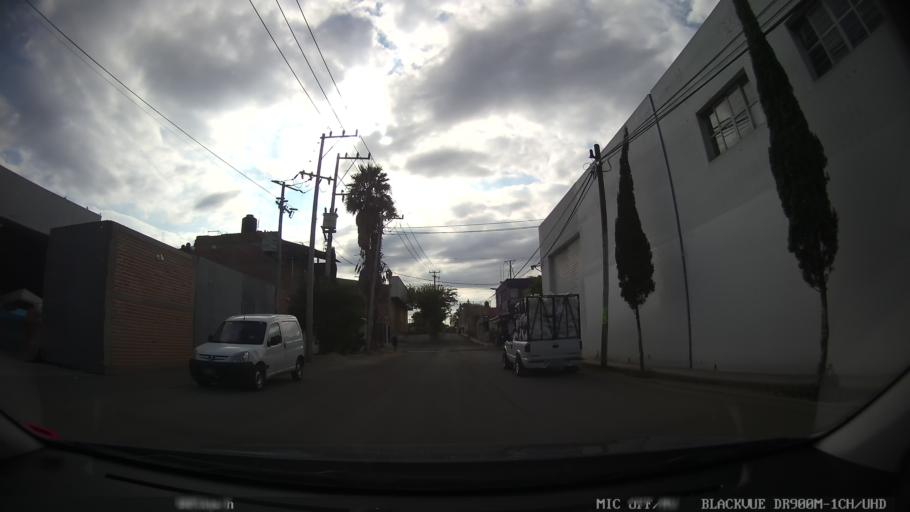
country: MX
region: Jalisco
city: Tonala
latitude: 20.6718
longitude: -103.2381
